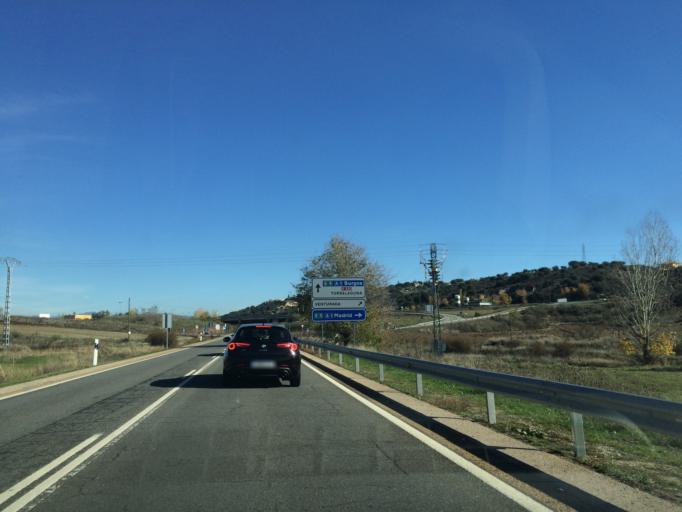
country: ES
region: Madrid
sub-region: Provincia de Madrid
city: Venturada
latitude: 40.7905
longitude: -3.6210
